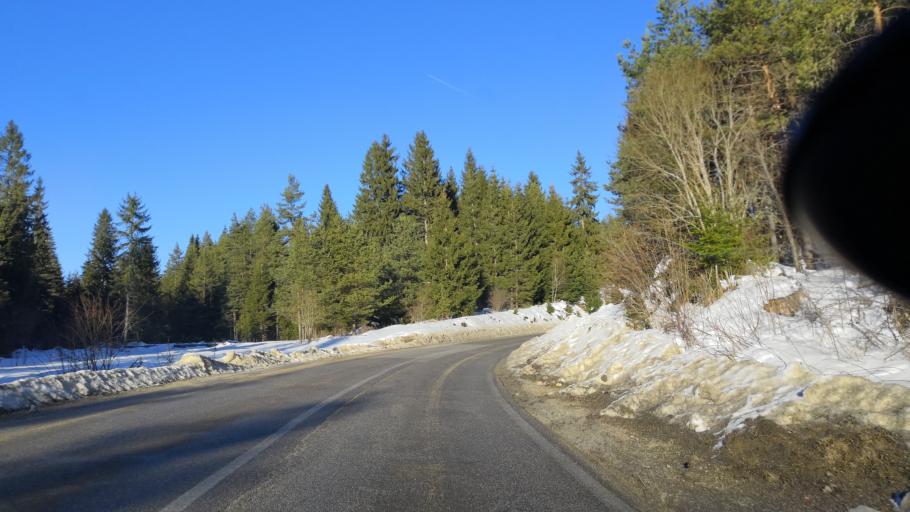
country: BA
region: Republika Srpska
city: Han Pijesak
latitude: 44.0242
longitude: 18.8819
